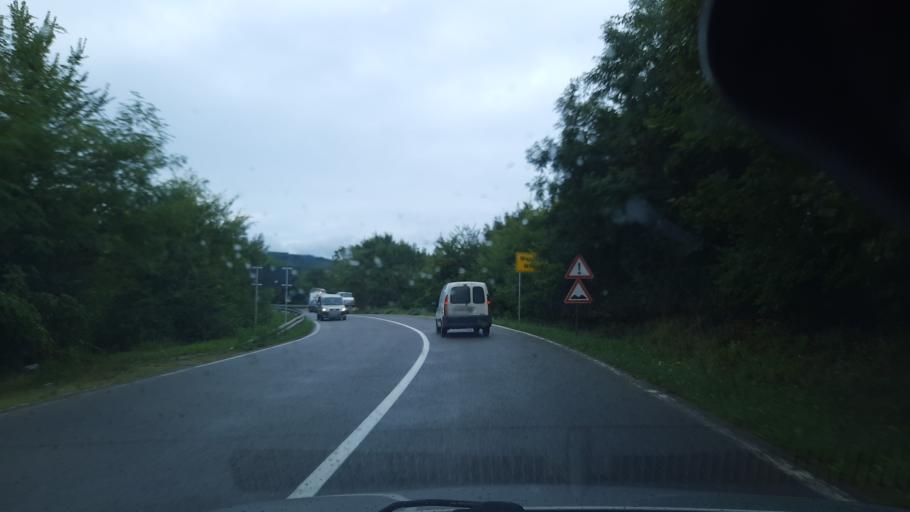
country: RS
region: Central Serbia
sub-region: Raski Okrug
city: Kraljevo
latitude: 43.7660
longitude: 20.8041
